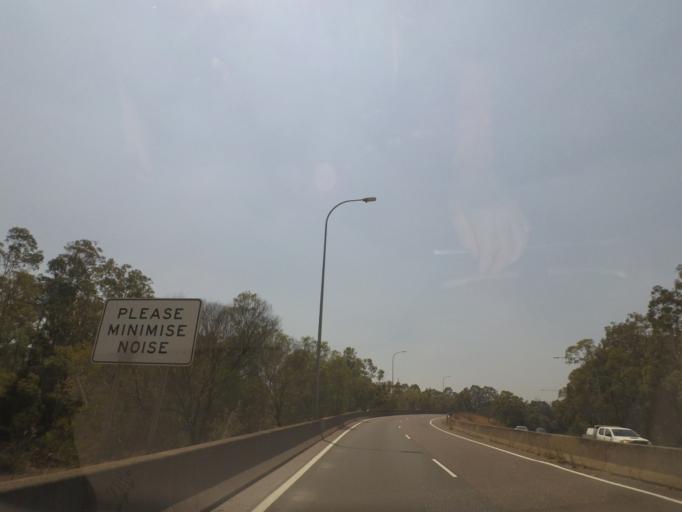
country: AU
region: New South Wales
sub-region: Newcastle
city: Beresfield
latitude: -32.8100
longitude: 151.6460
